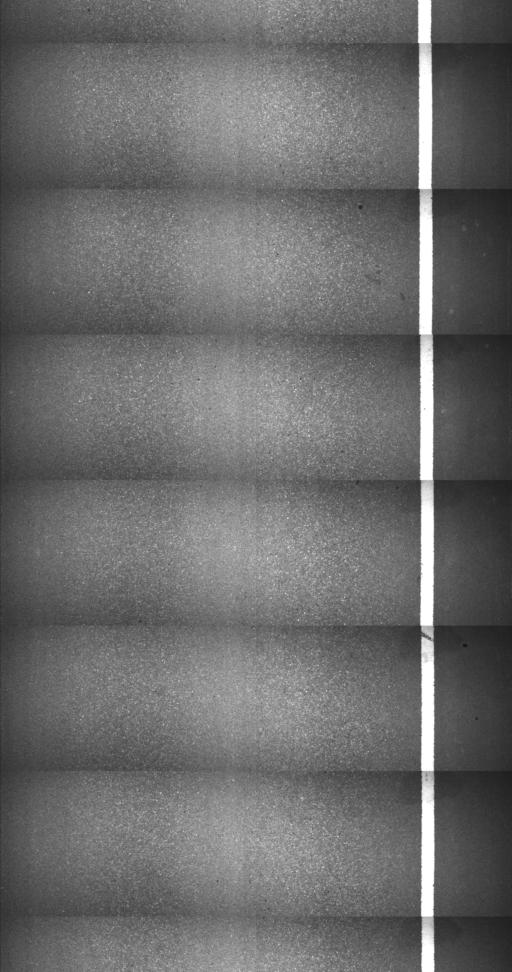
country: US
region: Vermont
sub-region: Chittenden County
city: Jericho
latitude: 44.5231
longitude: -73.0326
